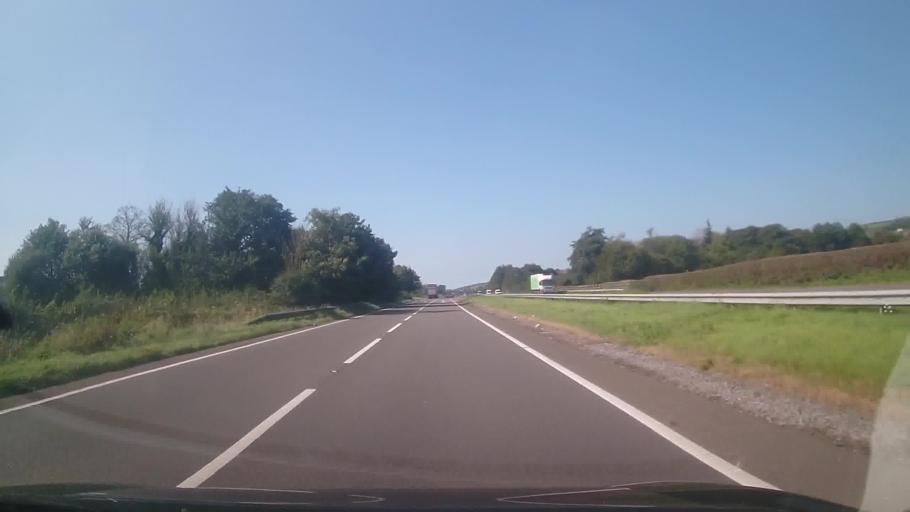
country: GB
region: Wales
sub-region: Carmarthenshire
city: Llangain
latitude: 51.8471
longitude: -4.3582
